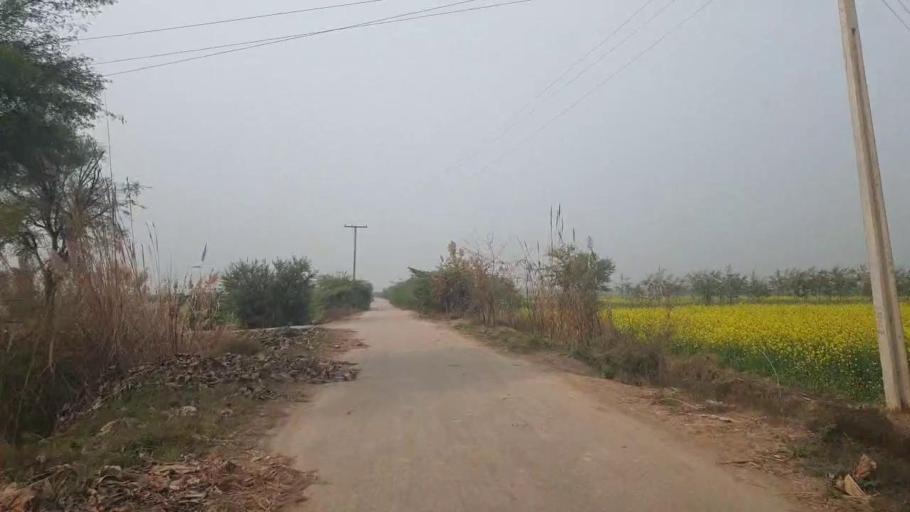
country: PK
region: Sindh
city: Tando Adam
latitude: 25.8169
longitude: 68.7149
